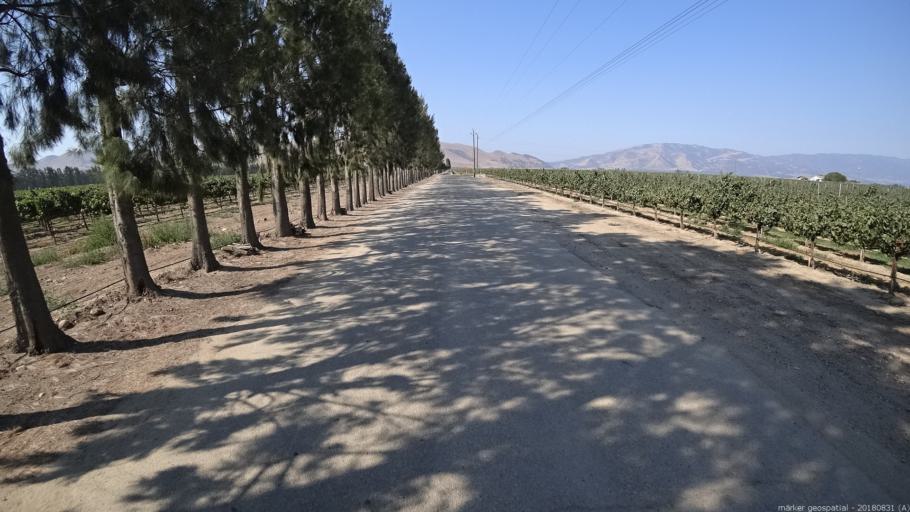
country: US
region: California
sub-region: Monterey County
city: Greenfield
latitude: 36.3013
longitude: -121.2427
